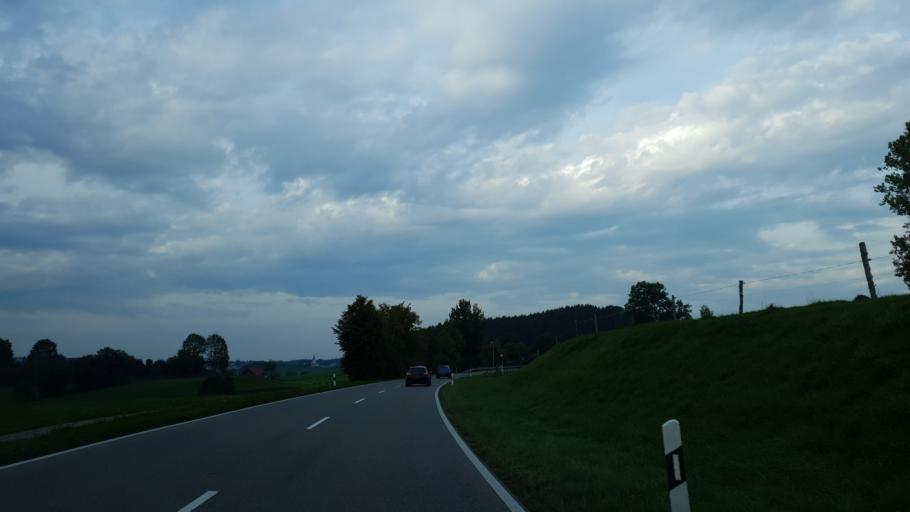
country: DE
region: Bavaria
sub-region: Swabia
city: Gestratz
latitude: 47.6715
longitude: 9.9515
